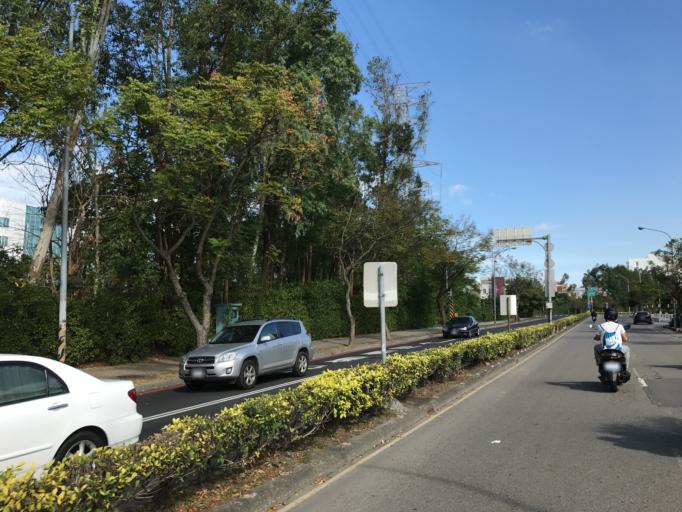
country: TW
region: Taiwan
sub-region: Hsinchu
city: Hsinchu
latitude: 24.7717
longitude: 121.0092
